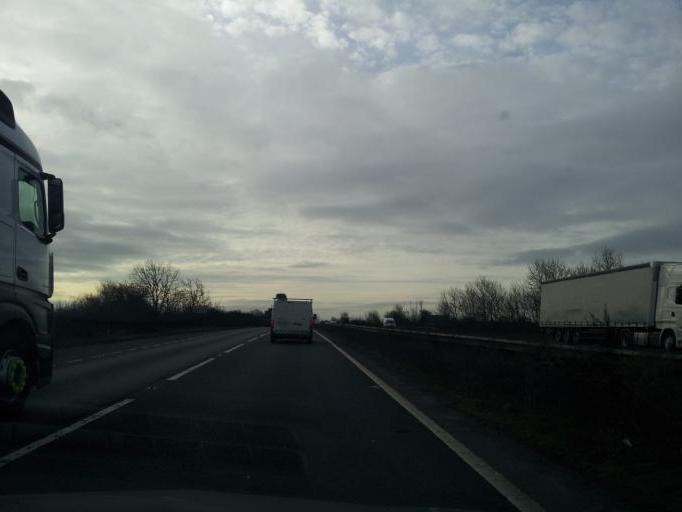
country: GB
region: England
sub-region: District of Rutland
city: Greetham
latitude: 52.7596
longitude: -0.6096
